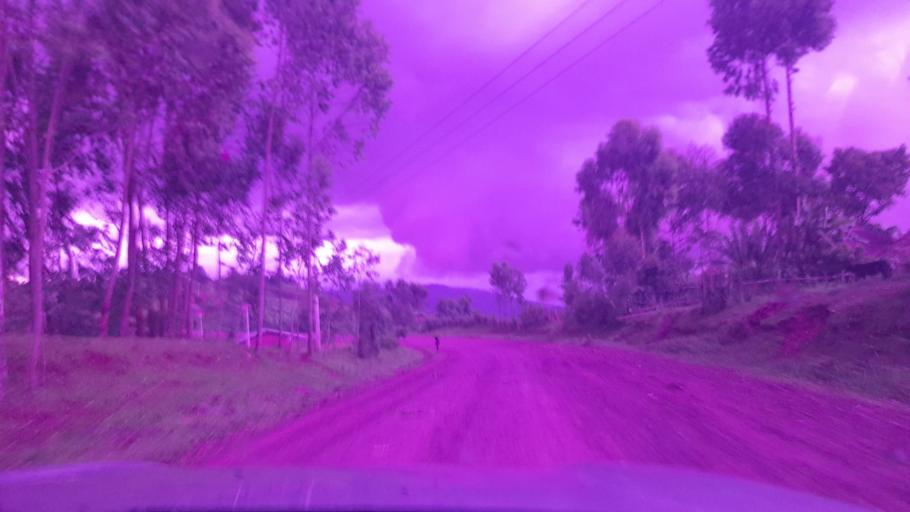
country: ET
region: Southern Nations, Nationalities, and People's Region
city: Mizan Teferi
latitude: 6.9068
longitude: 35.8426
